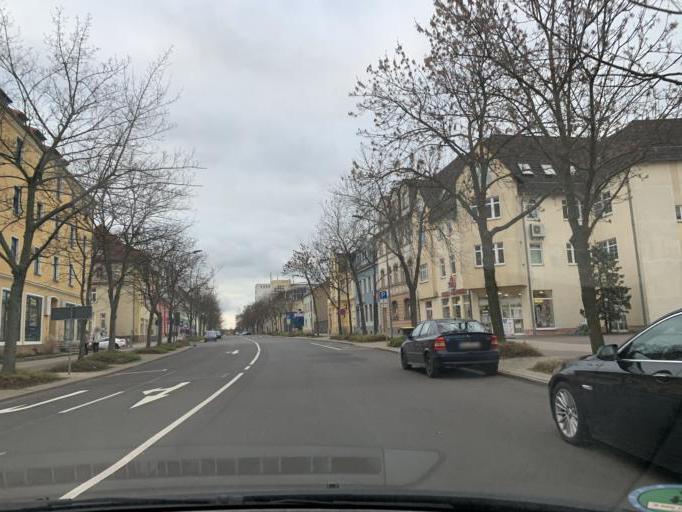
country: DE
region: Saxony-Anhalt
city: Merseburg
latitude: 51.3601
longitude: 11.9916
